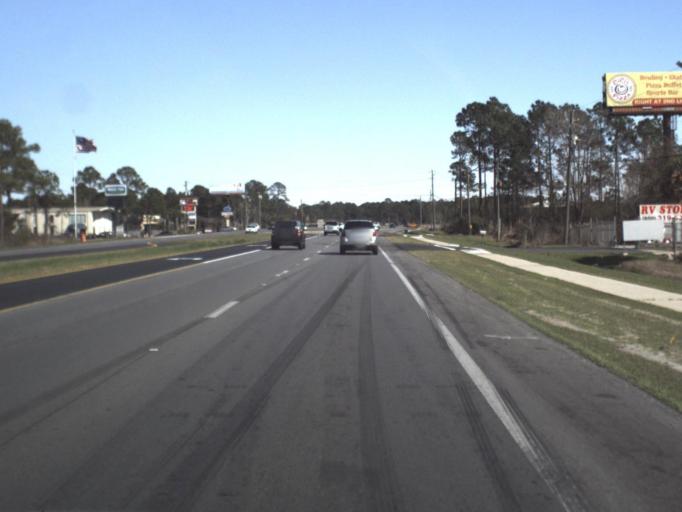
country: US
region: Florida
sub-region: Bay County
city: Panama City Beach
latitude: 30.2054
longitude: -85.8320
